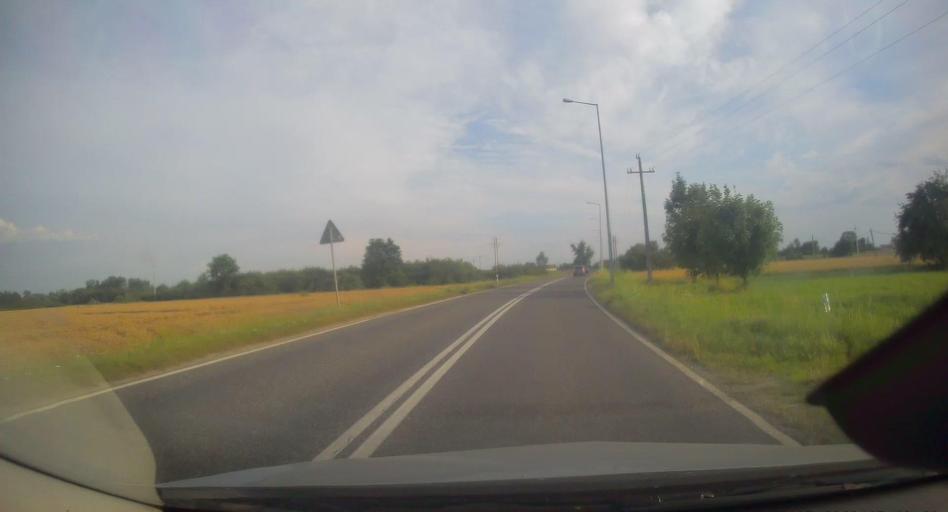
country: PL
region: Lesser Poland Voivodeship
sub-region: Powiat brzeski
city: Szczurowa
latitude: 50.1500
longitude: 20.6126
